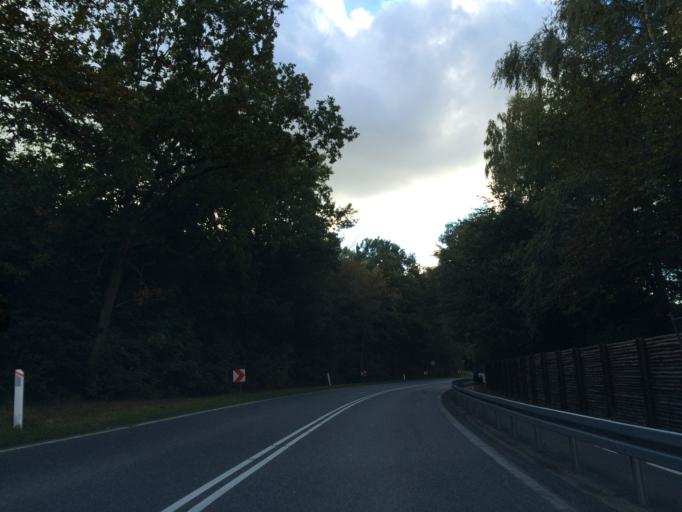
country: DK
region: Central Jutland
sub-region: Skanderborg Kommune
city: Ry
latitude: 56.0981
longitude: 9.7836
